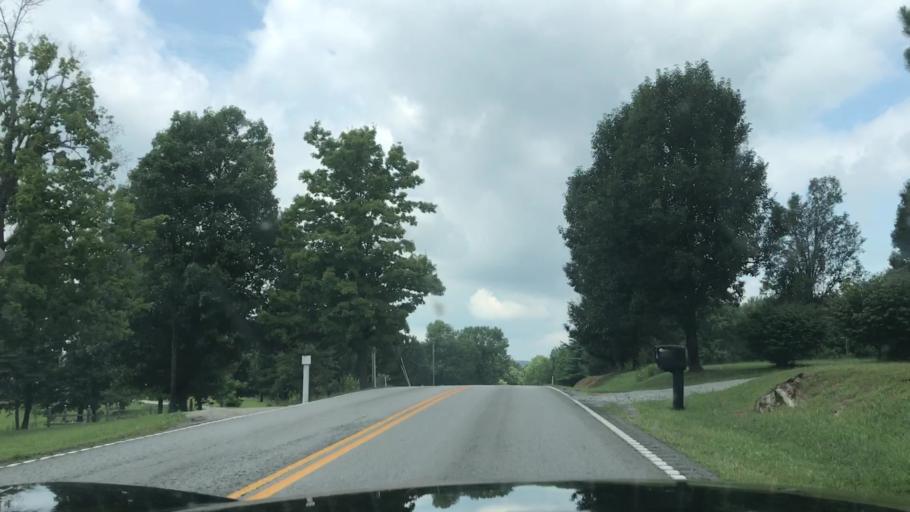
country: US
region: Kentucky
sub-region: Muhlenberg County
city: Greenville
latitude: 37.2028
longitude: -87.0957
